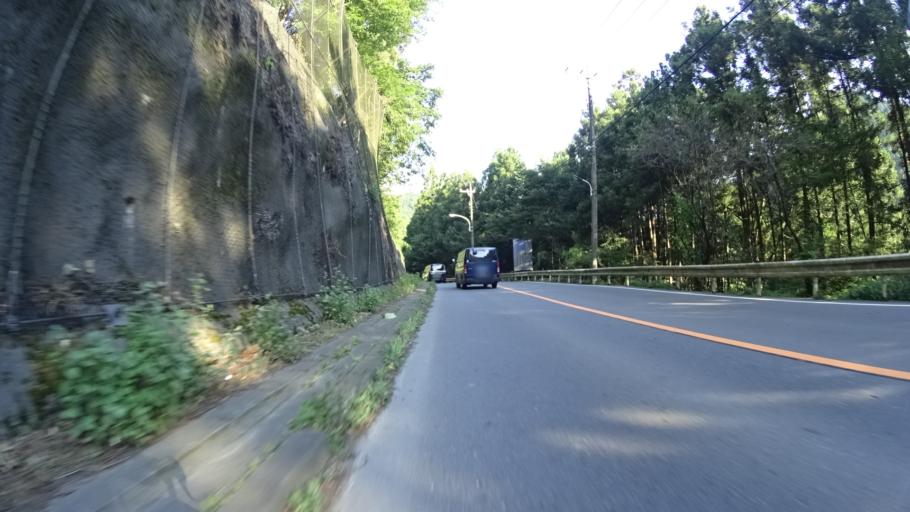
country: JP
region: Tokyo
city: Ome
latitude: 35.8052
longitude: 139.1706
